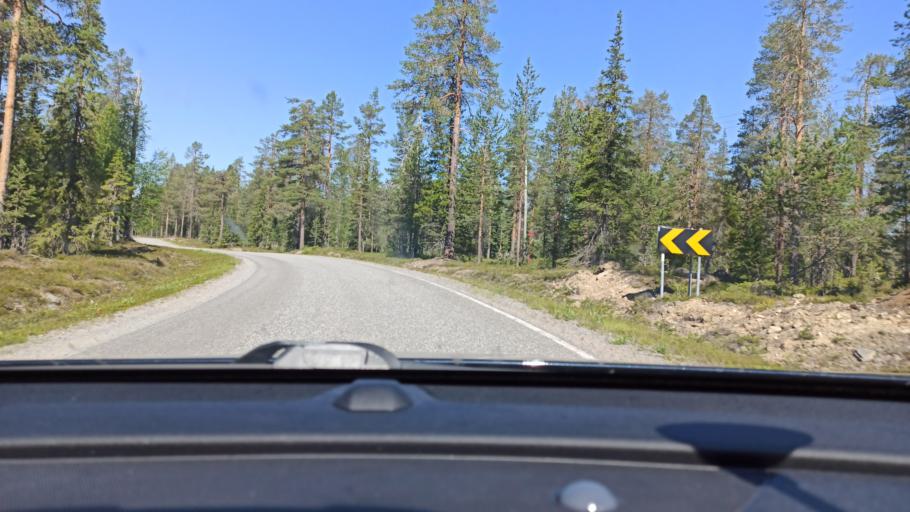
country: FI
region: Lapland
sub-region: Tunturi-Lappi
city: Kolari
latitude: 67.6687
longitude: 24.1585
